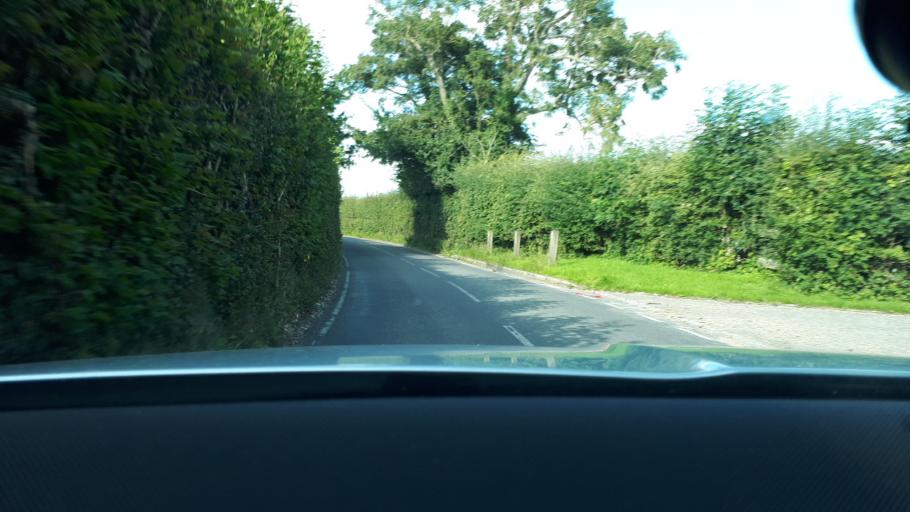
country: GB
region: England
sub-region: Kent
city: Biggin Hill
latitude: 51.3282
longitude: 0.0735
